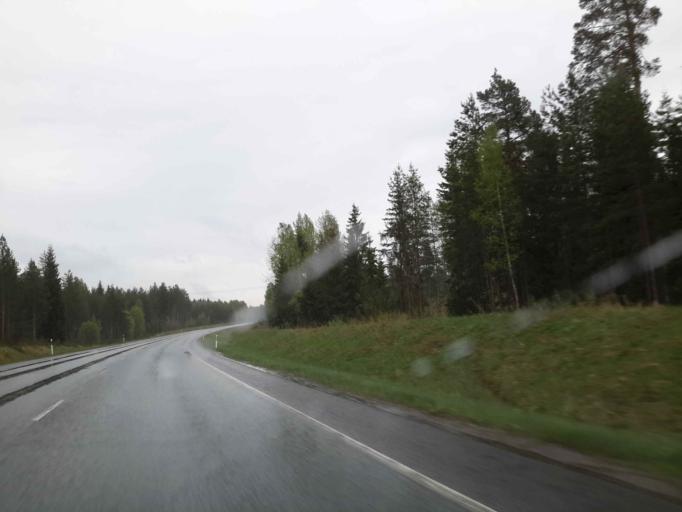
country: FI
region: Uusimaa
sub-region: Helsinki
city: Vihti
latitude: 60.3647
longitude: 24.3588
